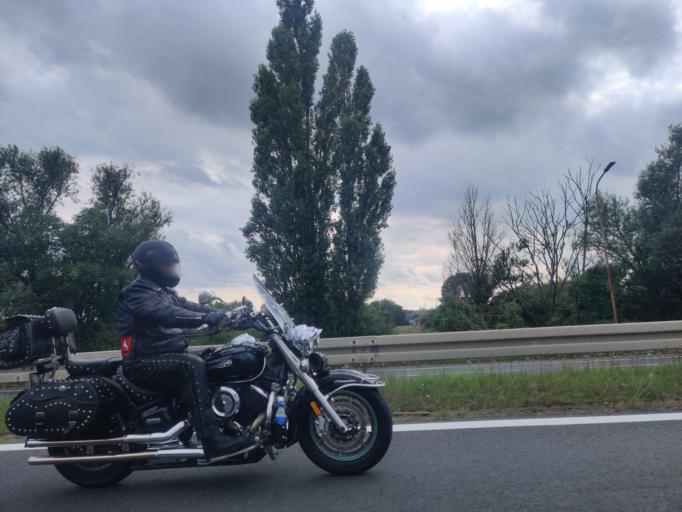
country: PL
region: Greater Poland Voivodeship
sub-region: Konin
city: Konin
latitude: 52.2093
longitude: 18.2639
